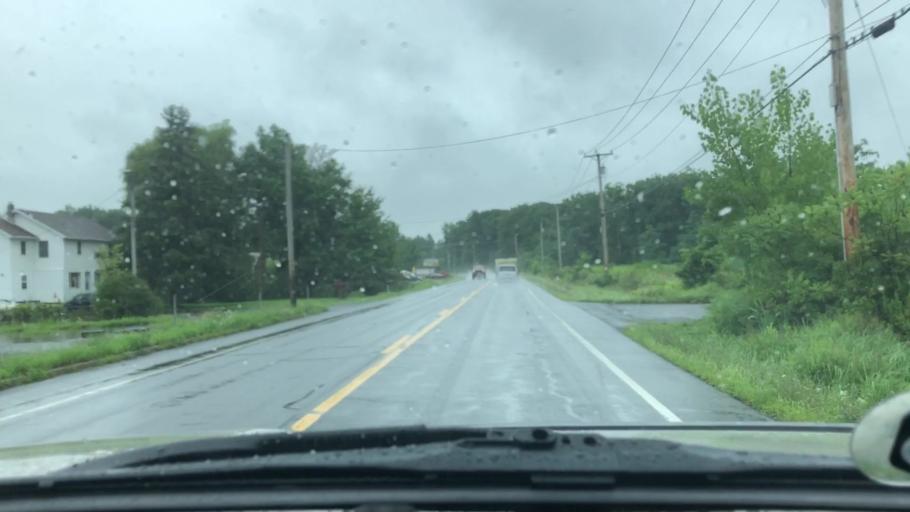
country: US
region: New York
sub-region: Greene County
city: Cairo
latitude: 42.2879
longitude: -73.9851
